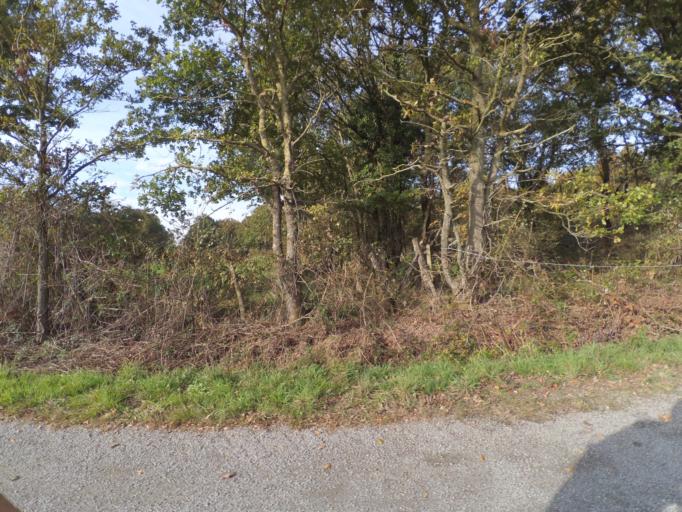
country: FR
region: Pays de la Loire
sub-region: Departement de la Vendee
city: Saint-Hilaire-de-Loulay
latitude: 47.0006
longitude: -1.3805
